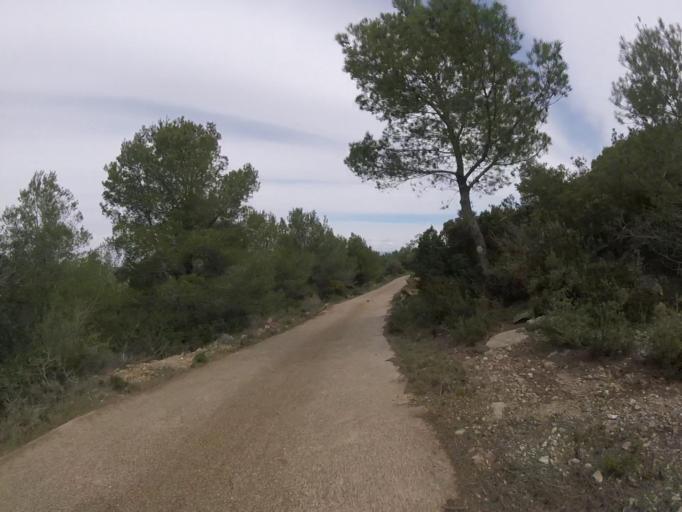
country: ES
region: Valencia
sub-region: Provincia de Castello
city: Cabanes
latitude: 40.1906
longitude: 0.0787
